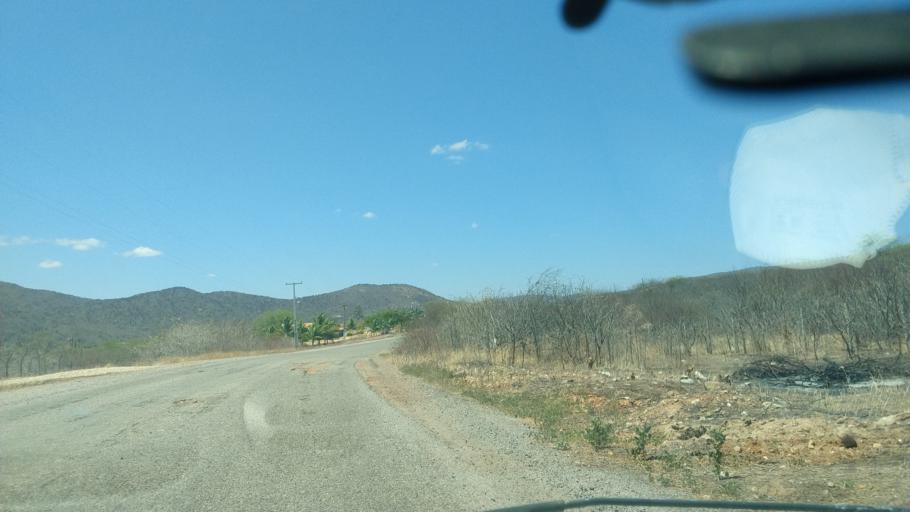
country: BR
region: Rio Grande do Norte
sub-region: Sao Tome
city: Sao Tome
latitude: -5.9767
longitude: -36.1447
